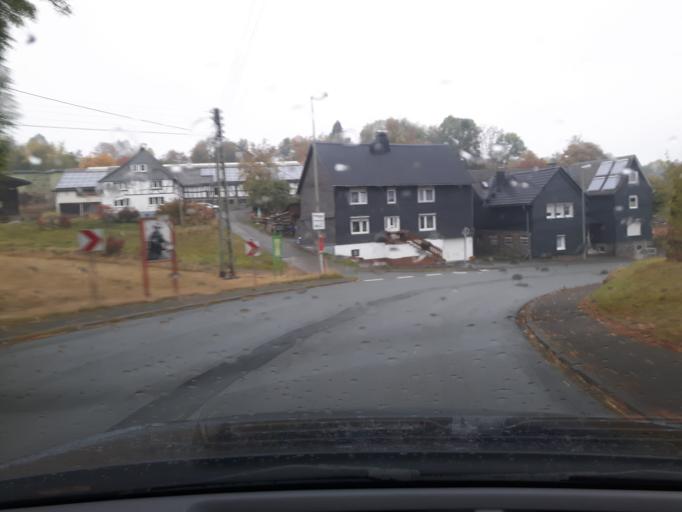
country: DE
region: North Rhine-Westphalia
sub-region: Regierungsbezirk Arnsberg
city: Bad Berleburg
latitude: 50.9911
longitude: 8.3915
